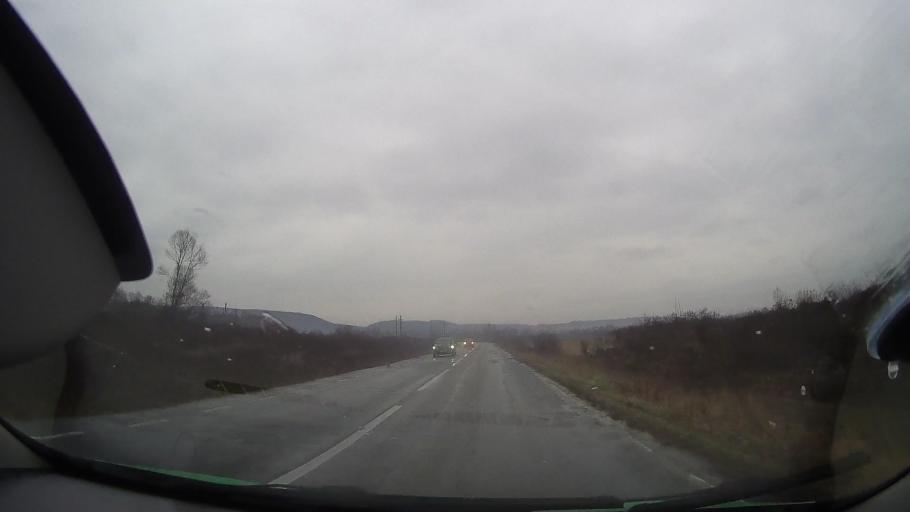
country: RO
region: Bihor
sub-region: Comuna Sambata
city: Sambata
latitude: 46.7840
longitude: 22.1909
